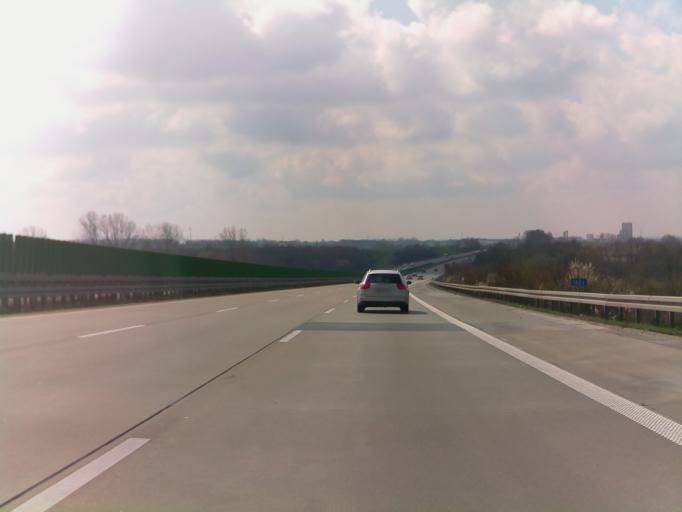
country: DE
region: Saxony-Anhalt
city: Osterfeld
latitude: 51.0695
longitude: 11.9542
